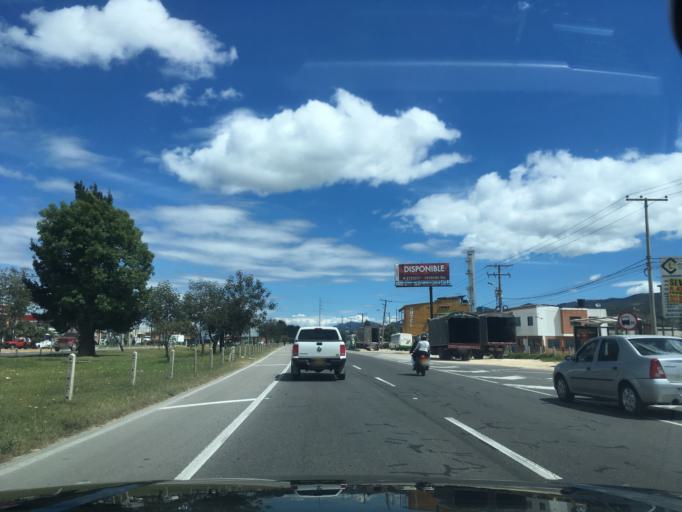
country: CO
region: Cundinamarca
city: Sopo
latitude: 4.9463
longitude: -73.9523
